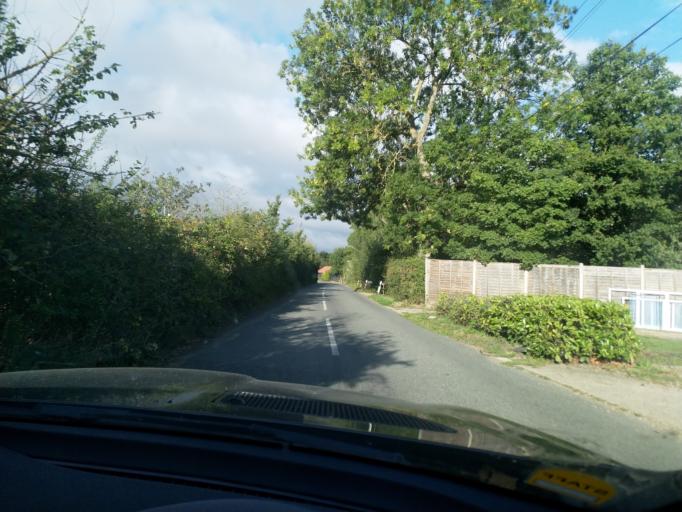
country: GB
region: England
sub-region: Suffolk
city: Elmswell
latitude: 52.2340
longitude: 0.9504
